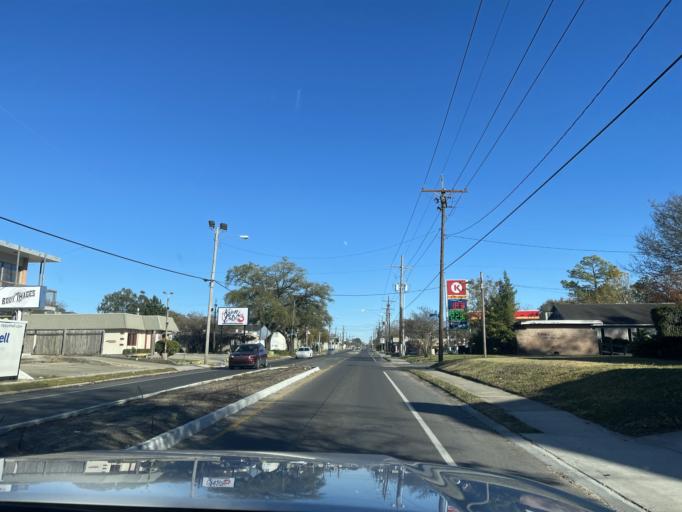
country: US
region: Louisiana
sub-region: East Baton Rouge Parish
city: Baton Rouge
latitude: 30.4442
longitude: -91.1529
